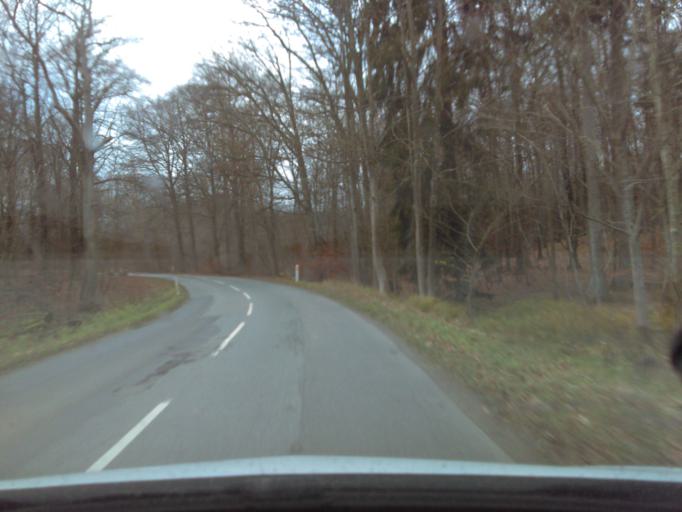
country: DK
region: Capital Region
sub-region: Fureso Kommune
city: Vaerlose
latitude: 55.7605
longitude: 12.3753
